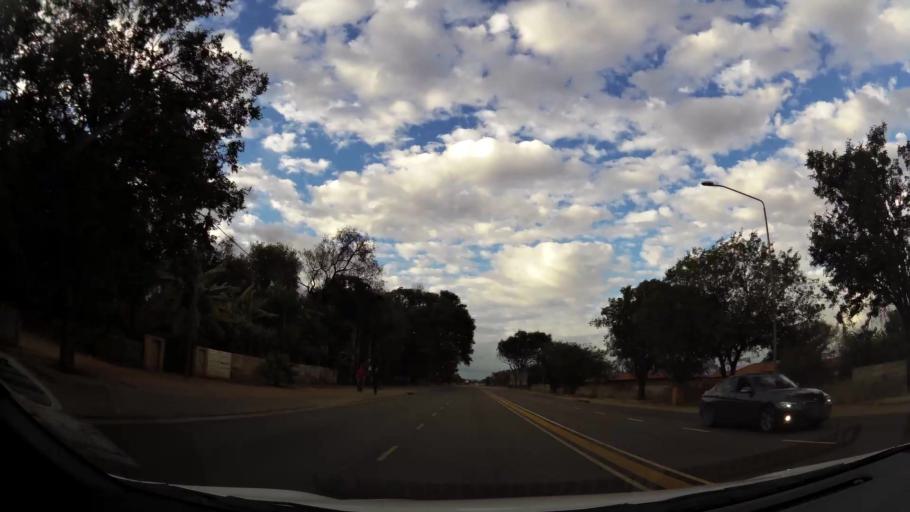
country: ZA
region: Limpopo
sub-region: Waterberg District Municipality
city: Modimolle
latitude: -24.5110
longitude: 28.7229
